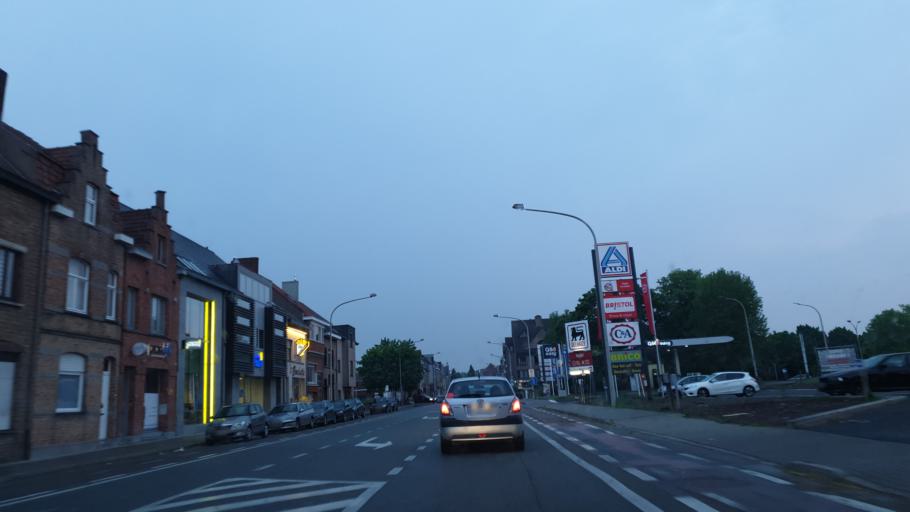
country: BE
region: Flanders
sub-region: Provincie West-Vlaanderen
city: Ieper
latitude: 50.8537
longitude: 2.8745
